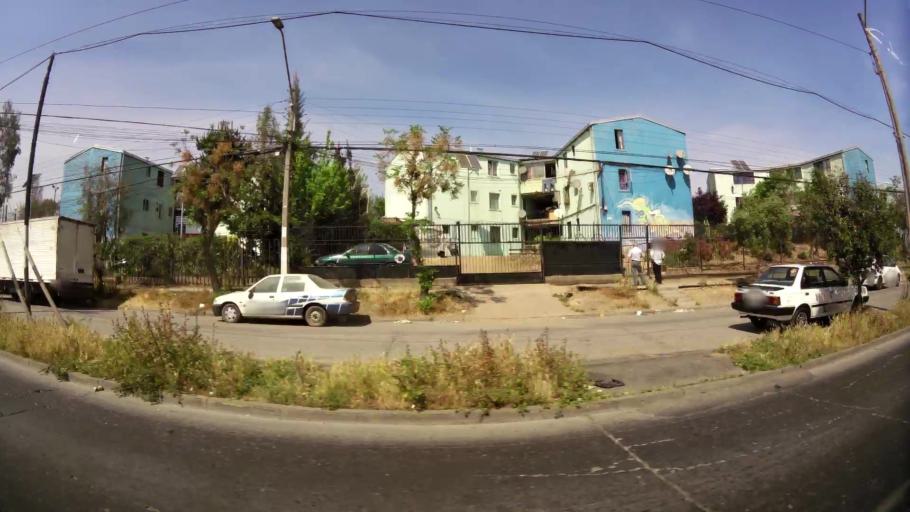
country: CL
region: Santiago Metropolitan
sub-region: Provincia de Santiago
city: Lo Prado
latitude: -33.4447
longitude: -70.7351
